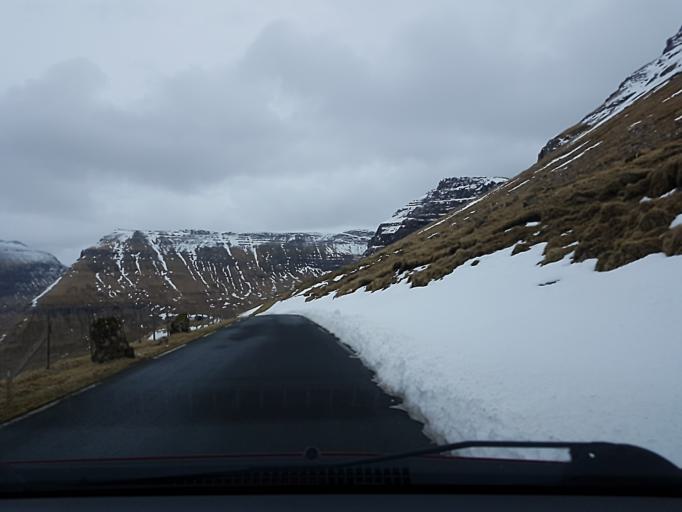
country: FO
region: Streymoy
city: Kollafjordhur
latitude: 62.0113
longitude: -6.9096
